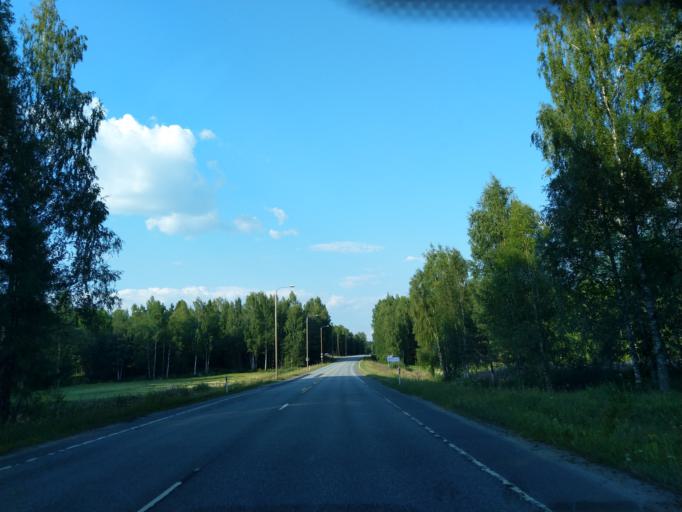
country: FI
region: Satakunta
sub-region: Pori
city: Laengelmaeki
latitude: 61.7482
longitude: 22.1058
